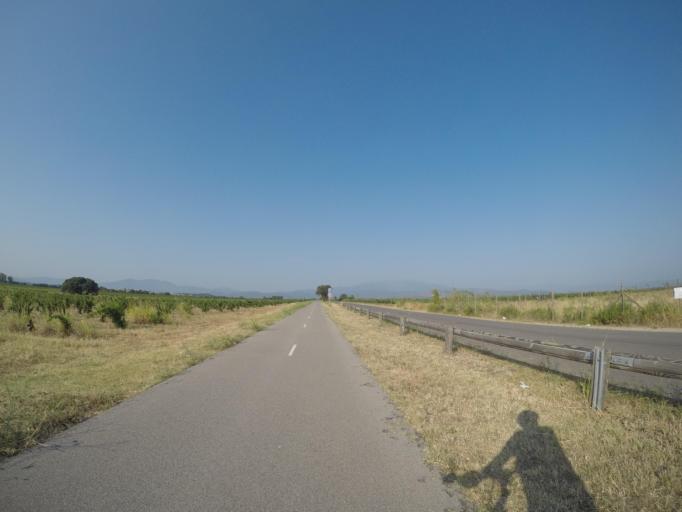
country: FR
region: Languedoc-Roussillon
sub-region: Departement des Pyrenees-Orientales
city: Canohes
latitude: 42.6457
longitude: 2.8188
